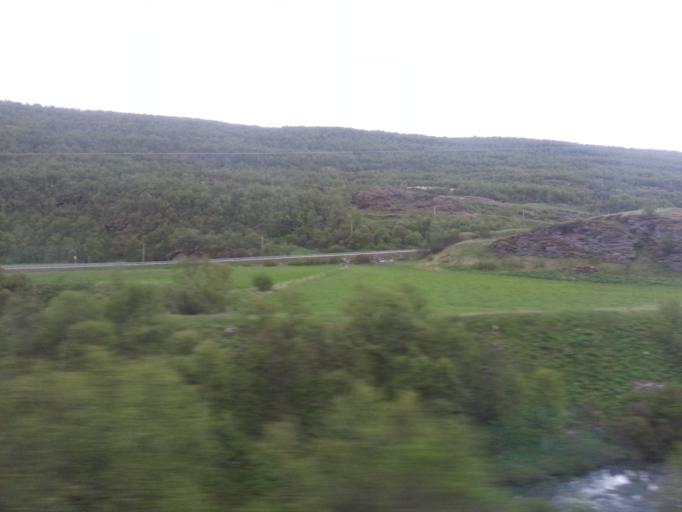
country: NO
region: Sor-Trondelag
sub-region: Oppdal
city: Oppdal
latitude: 62.3061
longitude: 9.6041
